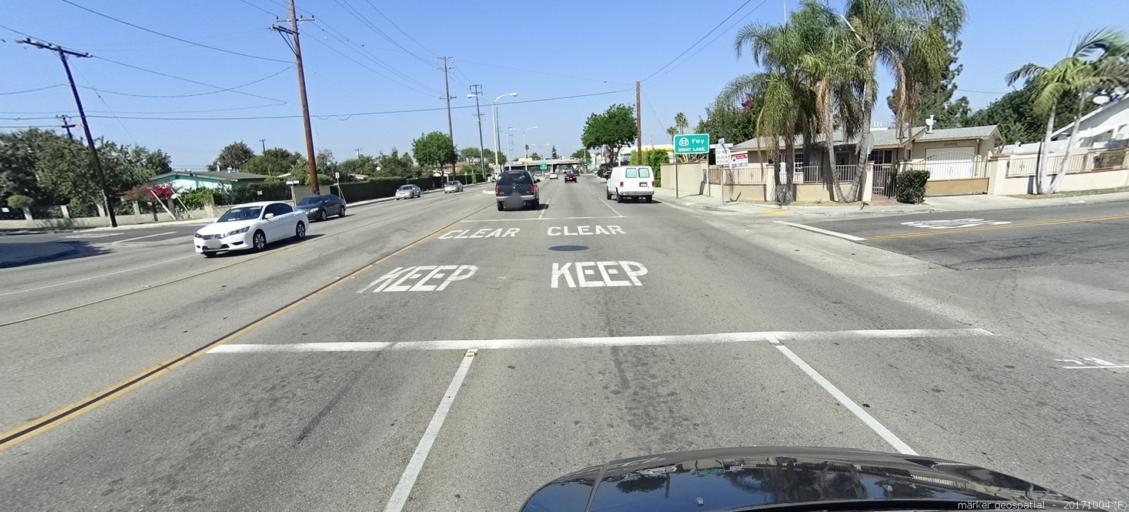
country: US
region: California
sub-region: Orange County
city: Garden Grove
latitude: 33.7634
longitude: -117.9376
